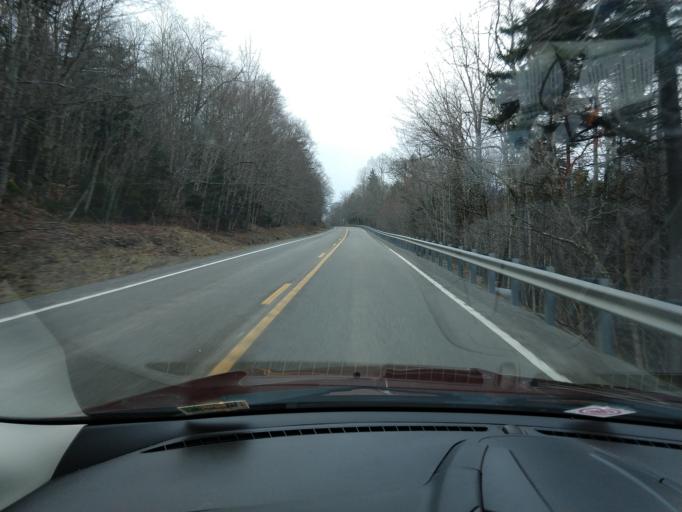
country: US
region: West Virginia
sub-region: Randolph County
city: Elkins
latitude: 38.6300
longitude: -79.9106
